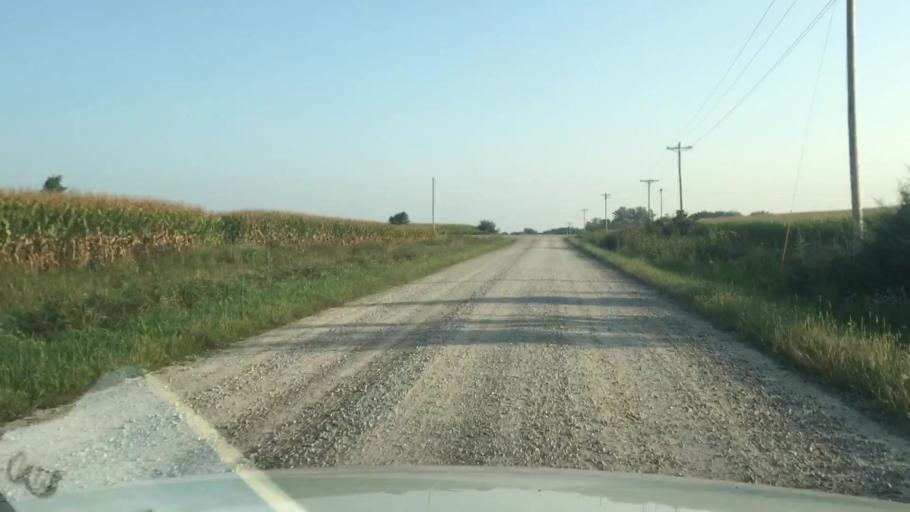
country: US
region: Iowa
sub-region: Story County
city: Huxley
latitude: 41.8977
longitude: -93.5809
